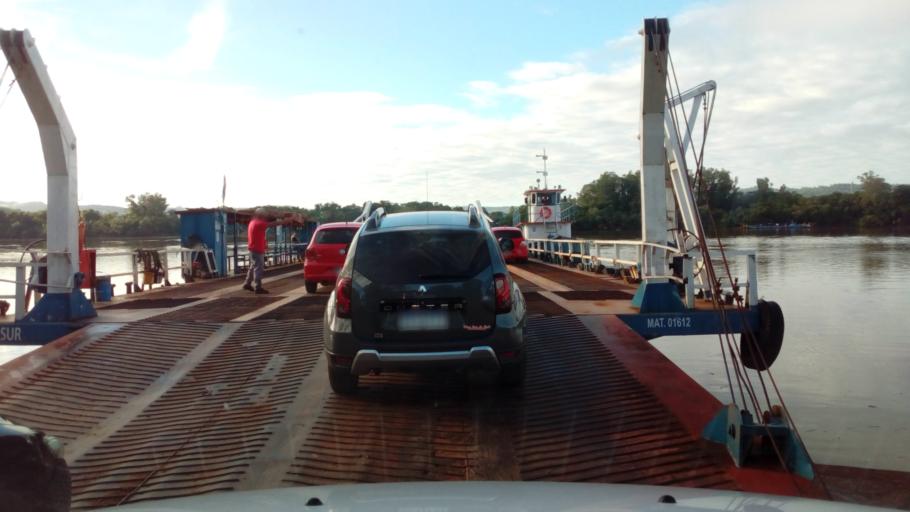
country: AR
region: Misiones
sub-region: Departamento de San Javier
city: San Javier
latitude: -27.8937
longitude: -55.1354
